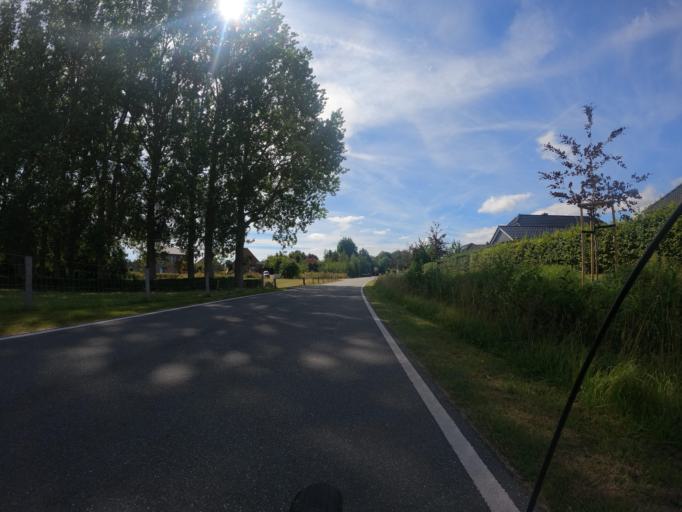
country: DE
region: Schleswig-Holstein
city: Steinbergkirche
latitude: 54.7597
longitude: 9.7619
